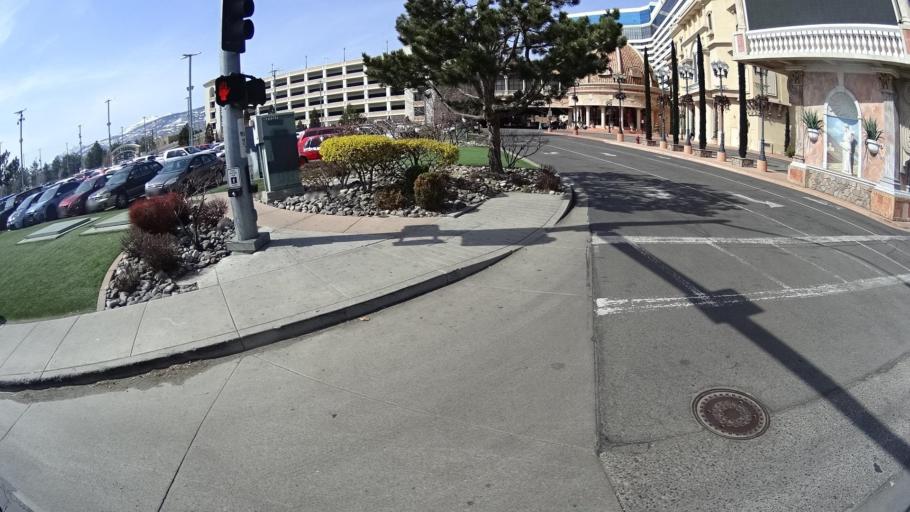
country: US
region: Nevada
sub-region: Washoe County
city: Reno
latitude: 39.4975
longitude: -119.7985
